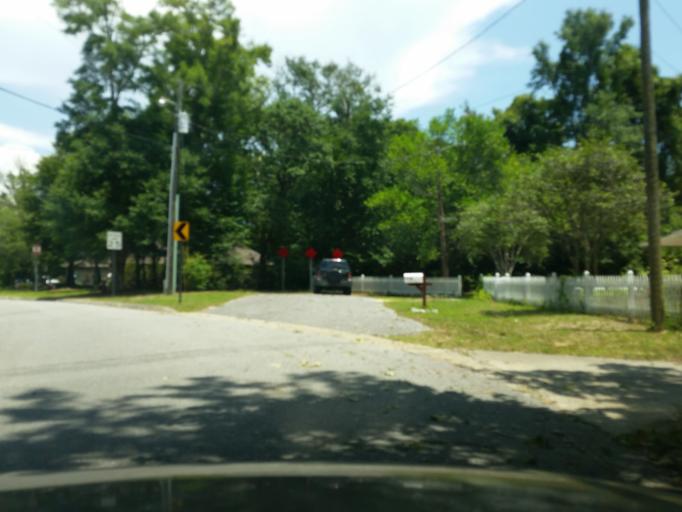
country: US
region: Florida
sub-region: Escambia County
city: Ferry Pass
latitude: 30.5332
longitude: -87.2017
